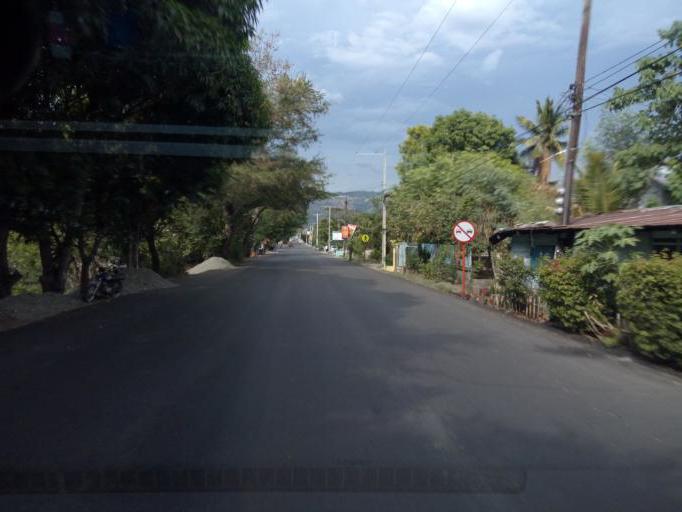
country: PH
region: Central Luzon
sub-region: Province of Nueva Ecija
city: Tayabo
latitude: 15.8233
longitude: 121.0105
